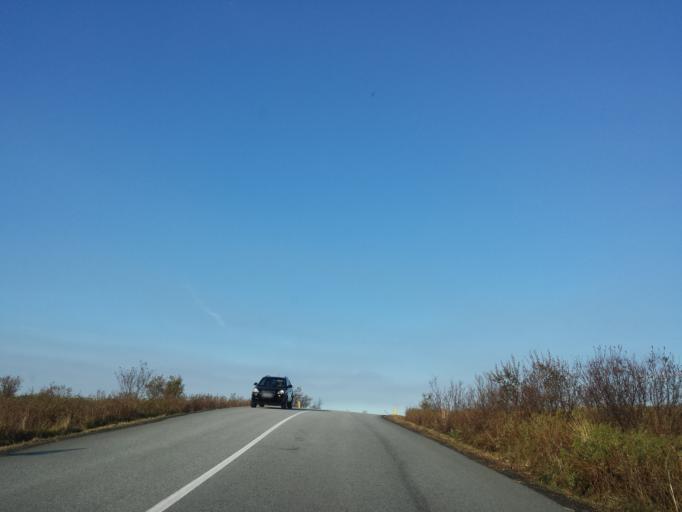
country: IS
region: Capital Region
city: Gardabaer
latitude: 64.0820
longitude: -21.8803
